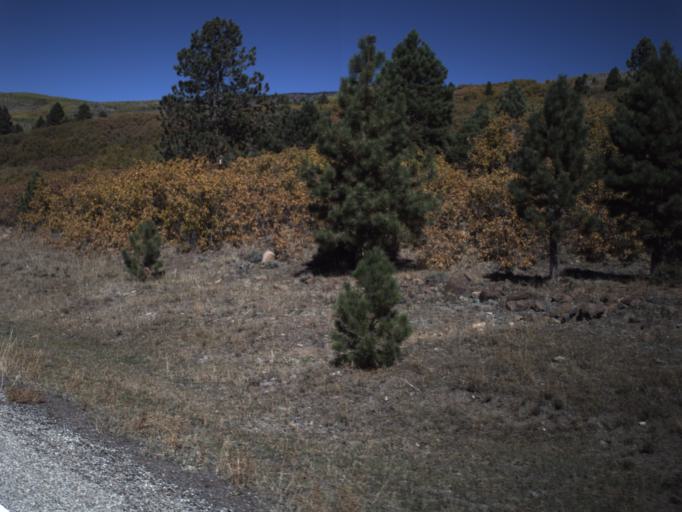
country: US
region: Utah
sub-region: Wayne County
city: Loa
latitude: 38.0071
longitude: -111.3948
